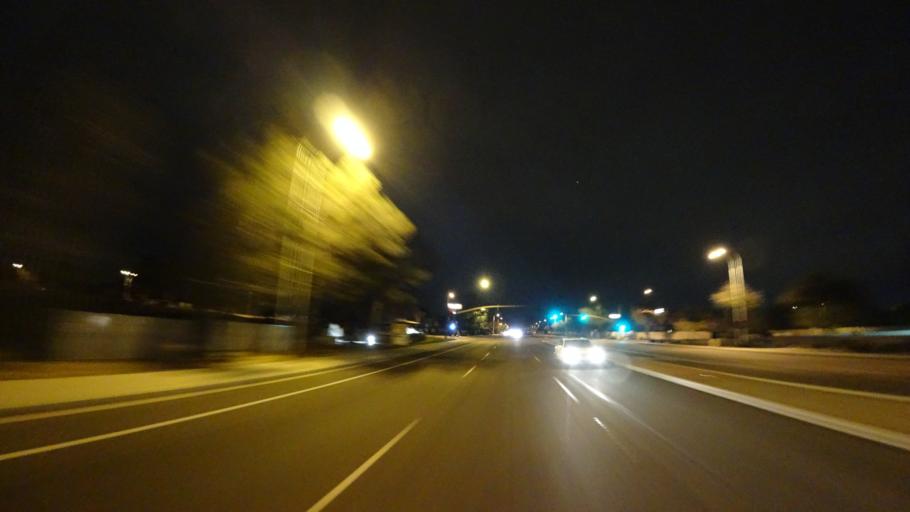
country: US
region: Arizona
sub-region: Maricopa County
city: Chandler
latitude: 33.3063
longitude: -111.8106
